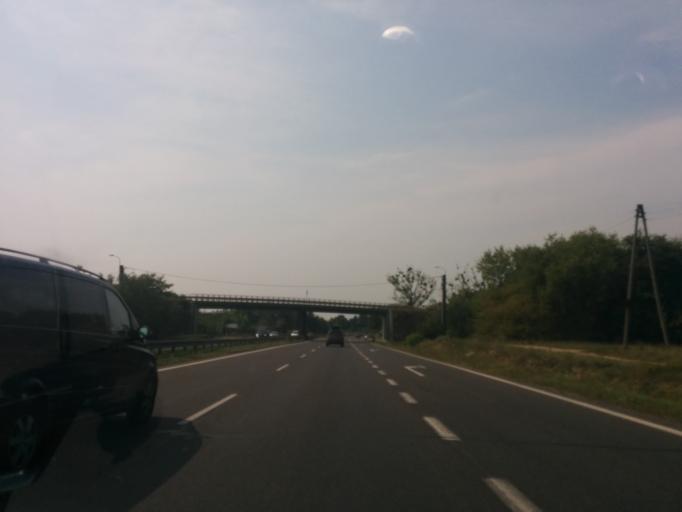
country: PL
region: Lodz Voivodeship
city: Zabia Wola
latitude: 52.0282
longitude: 20.6709
